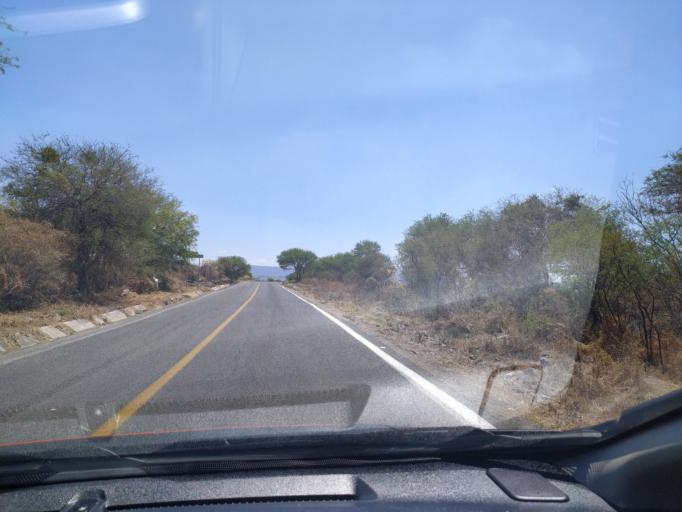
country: MX
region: Guanajuato
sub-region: San Francisco del Rincon
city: San Ignacio de Hidalgo
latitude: 20.7914
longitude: -101.8366
